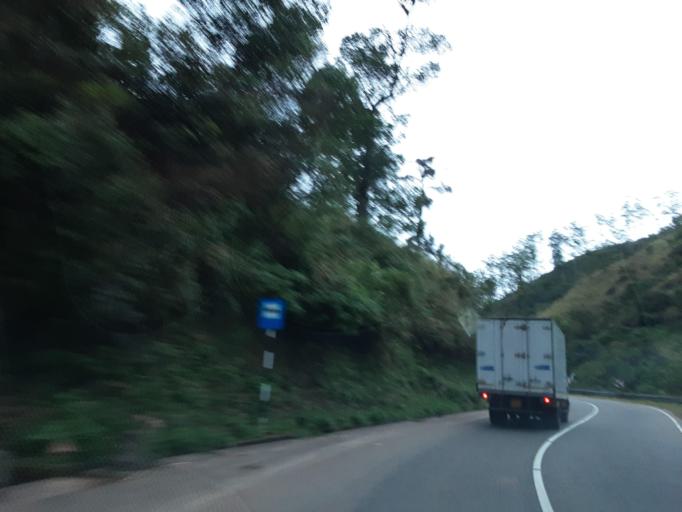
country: LK
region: Uva
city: Badulla
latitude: 6.9145
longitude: 80.9511
